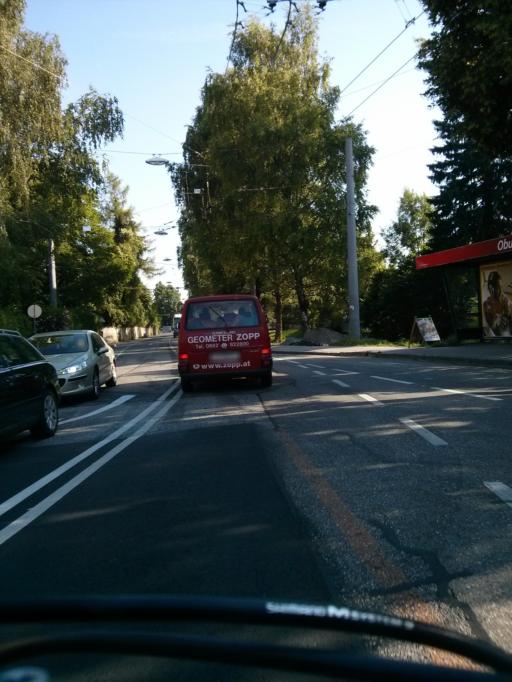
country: AT
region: Salzburg
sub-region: Salzburg Stadt
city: Salzburg
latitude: 47.8048
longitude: 13.0187
